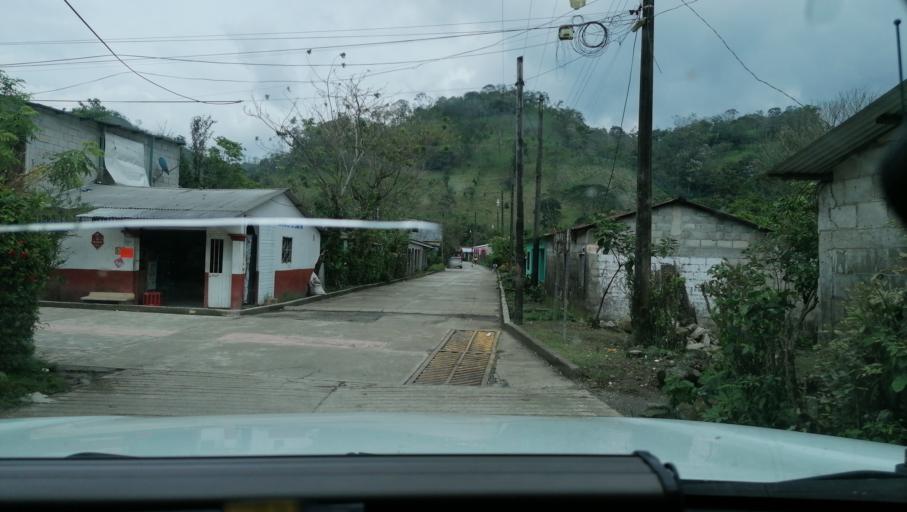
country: MX
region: Chiapas
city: Ixtacomitan
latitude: 17.3366
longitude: -93.1292
